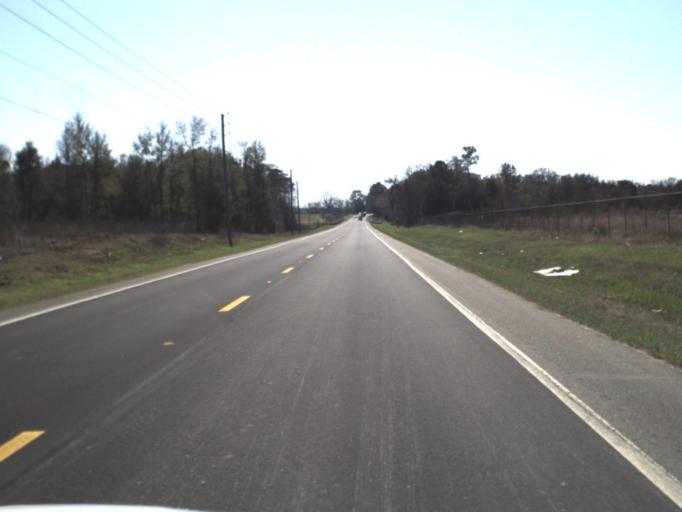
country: US
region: Florida
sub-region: Jackson County
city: Marianna
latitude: 30.6610
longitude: -85.1643
